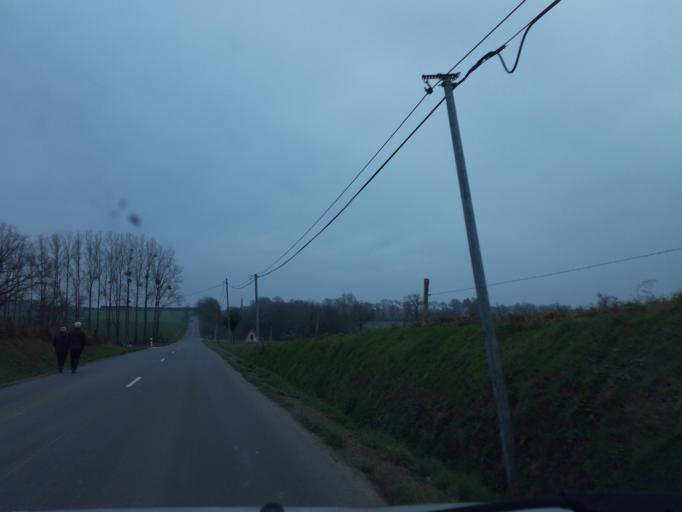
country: FR
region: Brittany
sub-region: Departement d'Ille-et-Vilaine
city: Gosne
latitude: 48.2544
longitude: -1.4556
